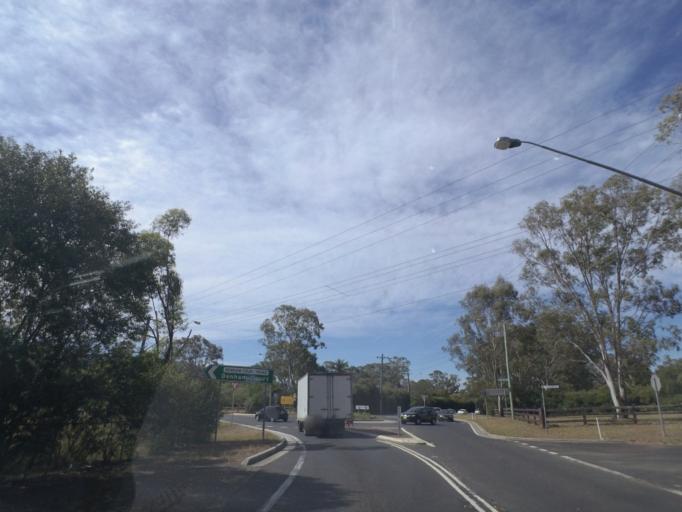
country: AU
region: New South Wales
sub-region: Campbelltown Municipality
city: Denham Court
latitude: -33.9847
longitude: 150.8444
